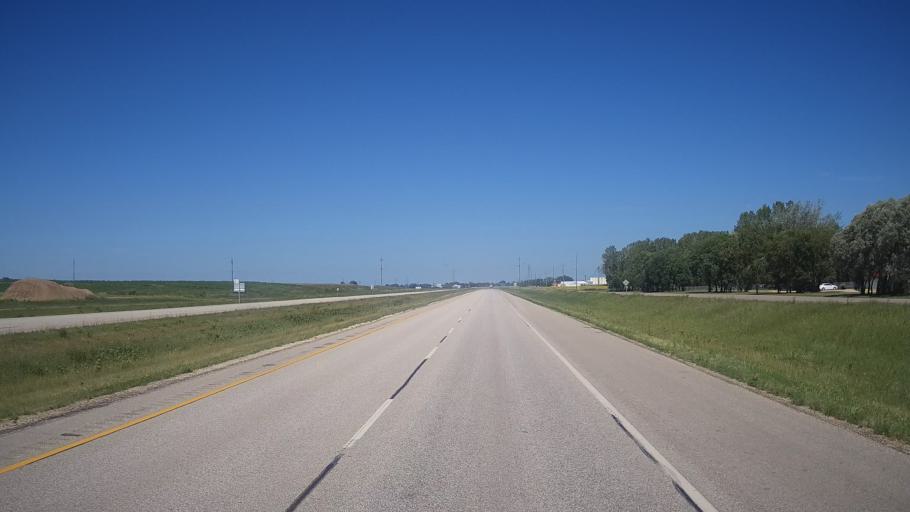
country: CA
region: Manitoba
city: Portage la Prairie
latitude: 49.9555
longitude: -98.3305
